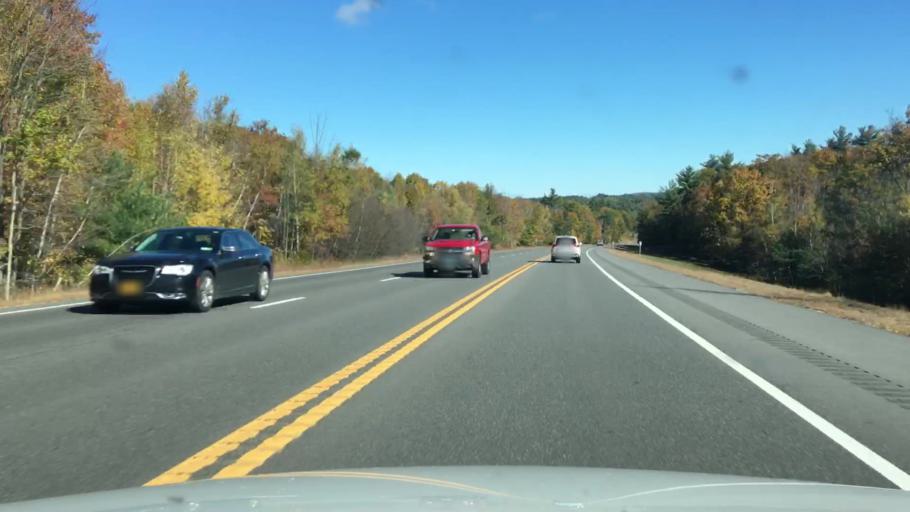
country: US
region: New Hampshire
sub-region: Strafford County
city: Farmington
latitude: 43.4421
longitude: -71.0043
